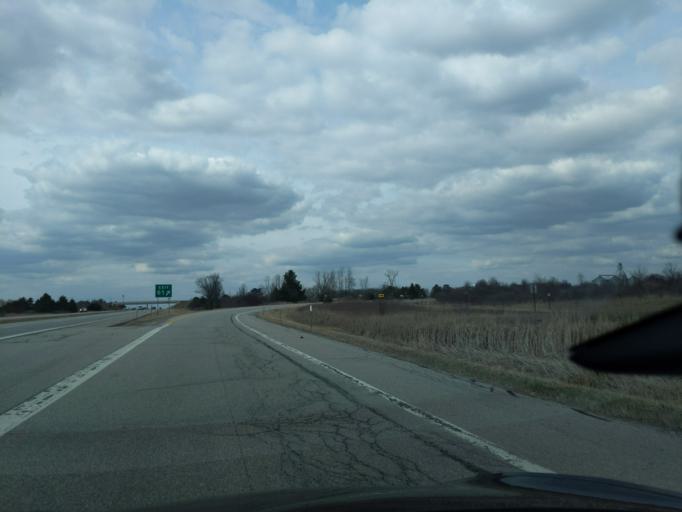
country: US
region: Michigan
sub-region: Ingham County
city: Mason
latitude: 42.5198
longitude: -84.4431
